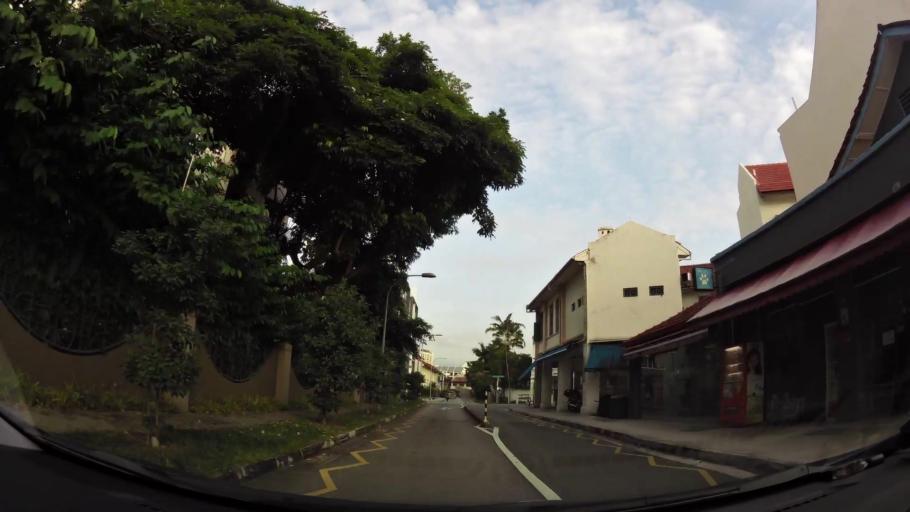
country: SG
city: Singapore
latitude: 1.3132
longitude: 103.9024
